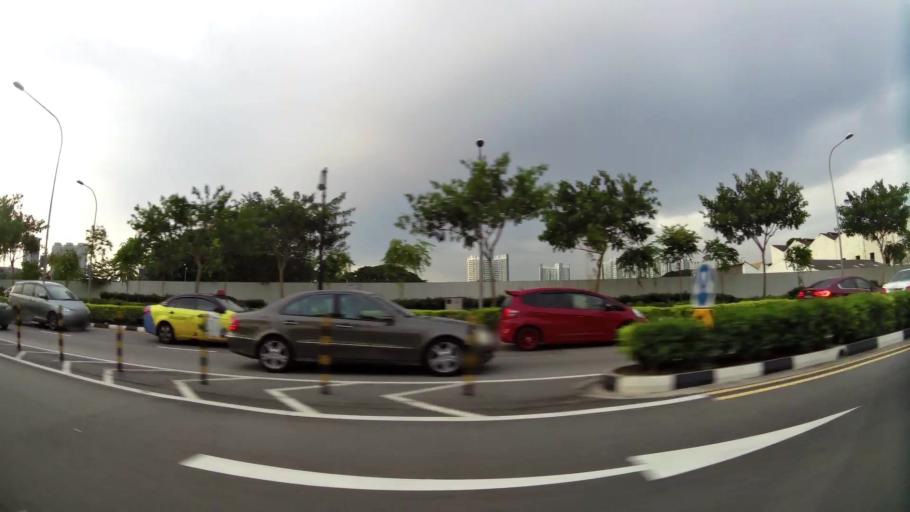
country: SG
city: Singapore
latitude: 1.3067
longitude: 103.8721
